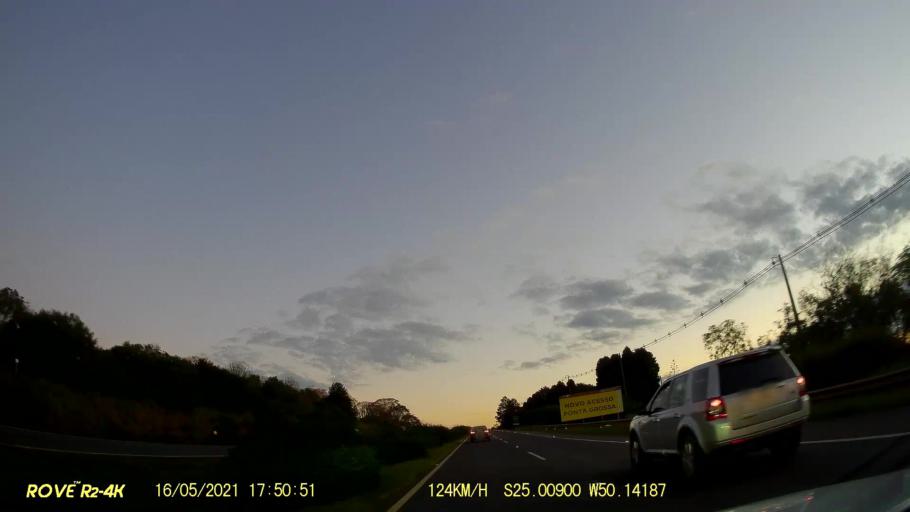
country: BR
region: Parana
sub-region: Carambei
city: Carambei
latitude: -25.0091
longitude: -50.1420
